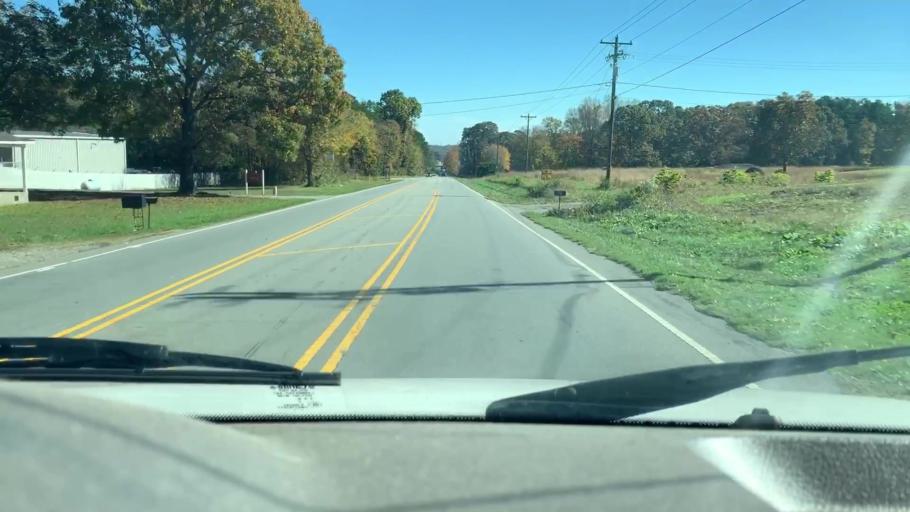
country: US
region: North Carolina
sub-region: Lincoln County
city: Lowesville
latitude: 35.4388
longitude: -80.9786
